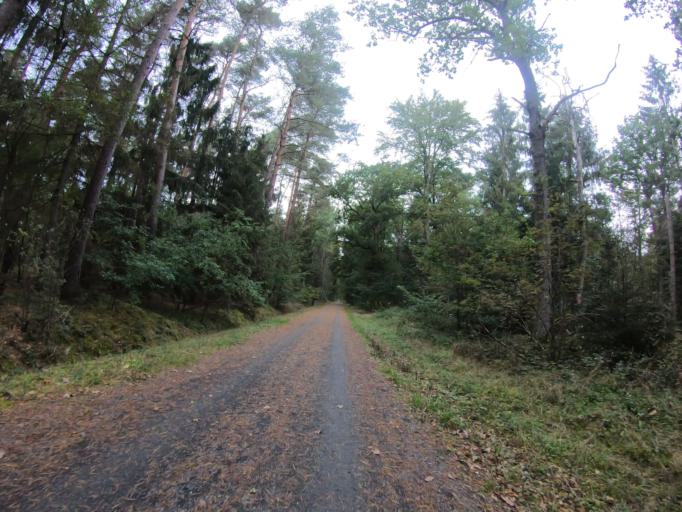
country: DE
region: Lower Saxony
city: Gifhorn
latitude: 52.4557
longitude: 10.5635
